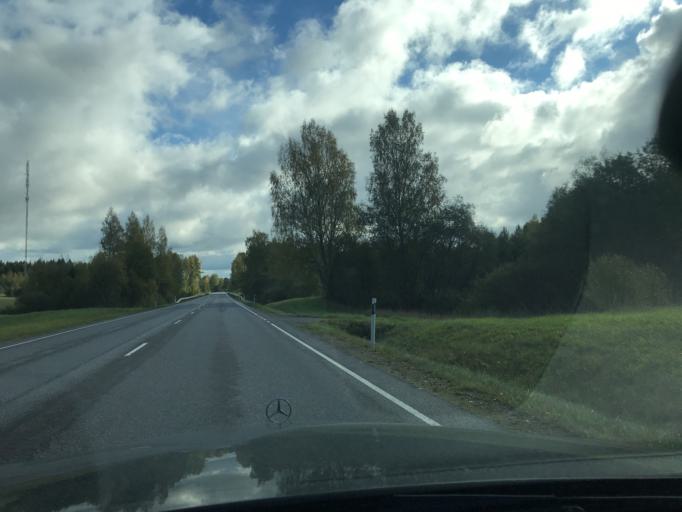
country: EE
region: Vorumaa
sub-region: Voru linn
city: Voru
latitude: 57.7722
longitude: 27.1457
